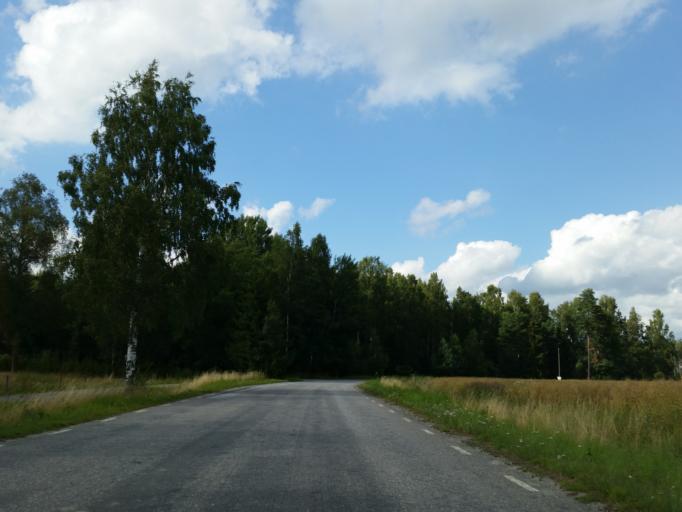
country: SE
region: Soedermanland
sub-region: Strangnas Kommun
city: Mariefred
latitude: 59.2204
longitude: 17.2951
